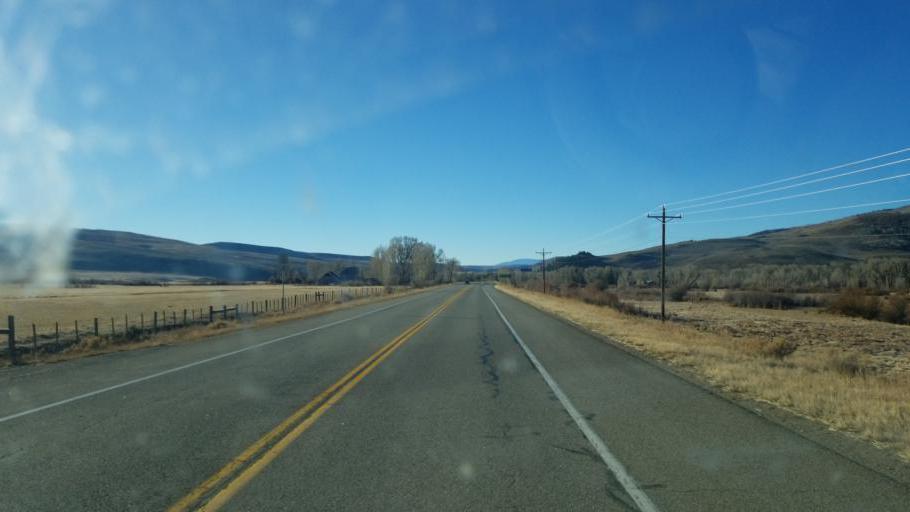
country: US
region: Colorado
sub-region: Gunnison County
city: Crested Butte
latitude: 38.7435
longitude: -106.8570
